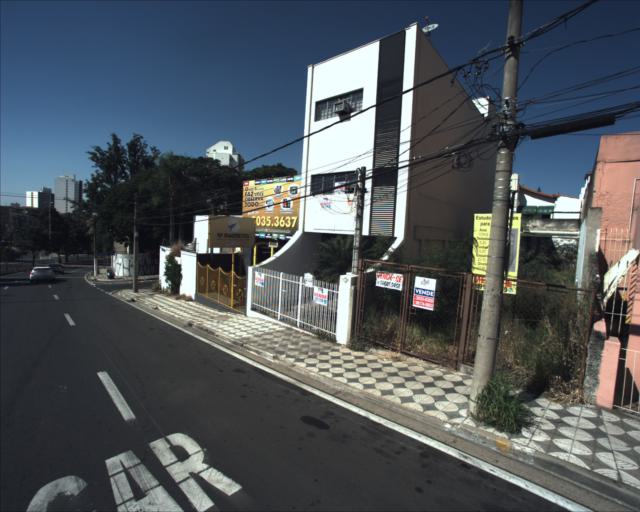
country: BR
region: Sao Paulo
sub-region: Sorocaba
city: Sorocaba
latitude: -23.5049
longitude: -47.4632
